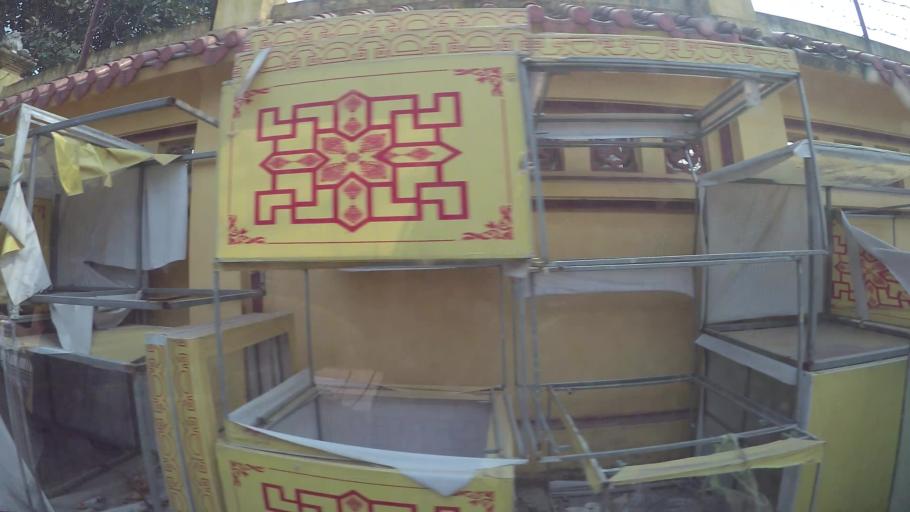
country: VN
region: Ha Noi
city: Van Dien
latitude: 20.9628
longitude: 105.8184
